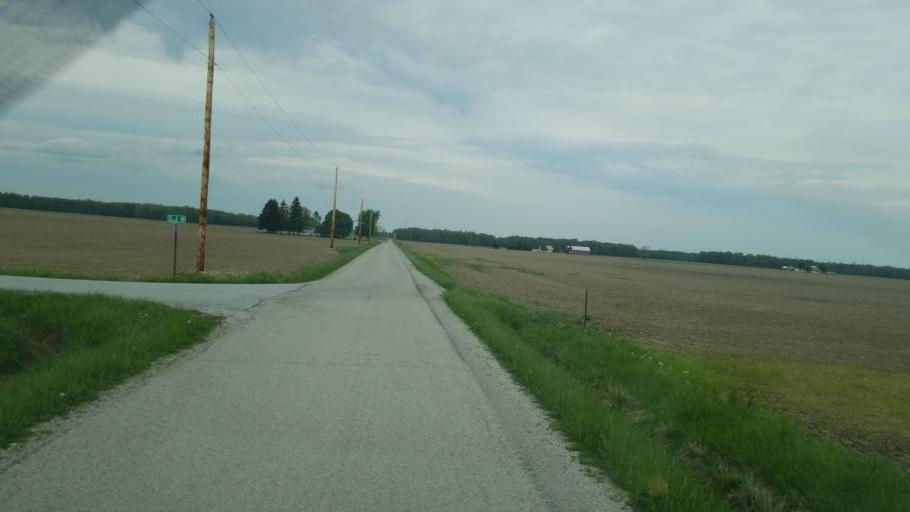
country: US
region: Ohio
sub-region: Huron County
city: Willard
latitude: 41.0224
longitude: -82.8621
